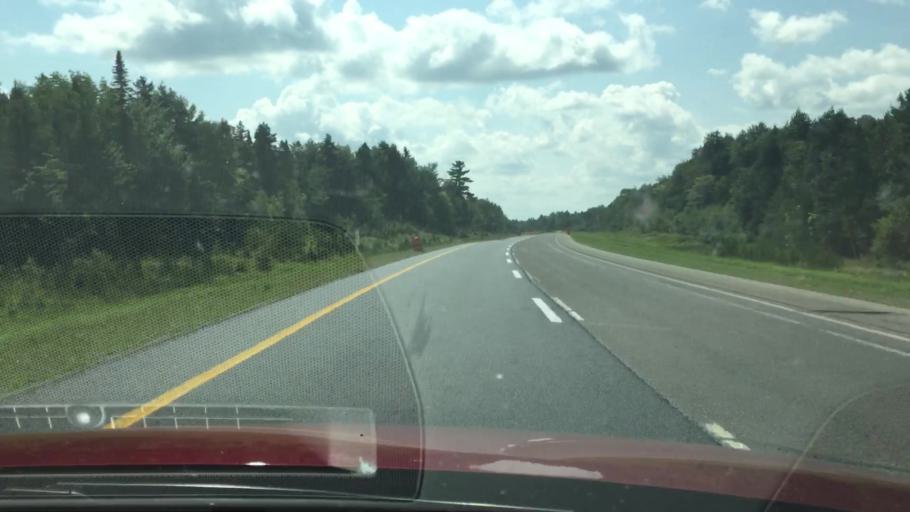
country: US
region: Maine
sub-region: Penobscot County
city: Medway
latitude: 45.7078
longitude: -68.4783
